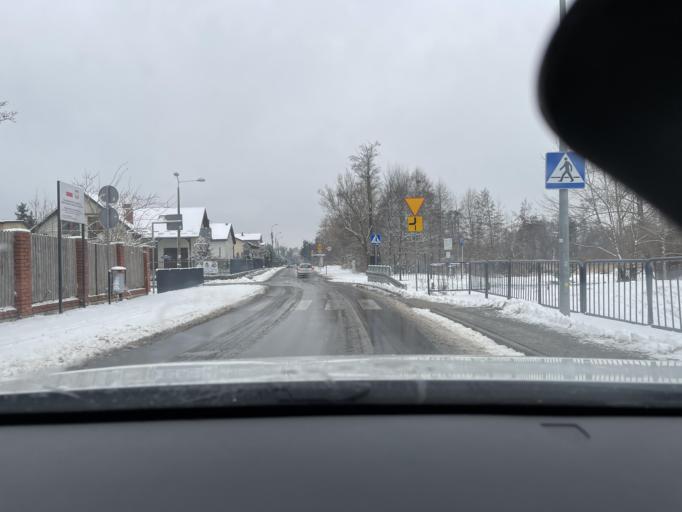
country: PL
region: Masovian Voivodeship
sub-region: Powiat zyrardowski
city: Zyrardow
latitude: 52.0425
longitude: 20.4462
